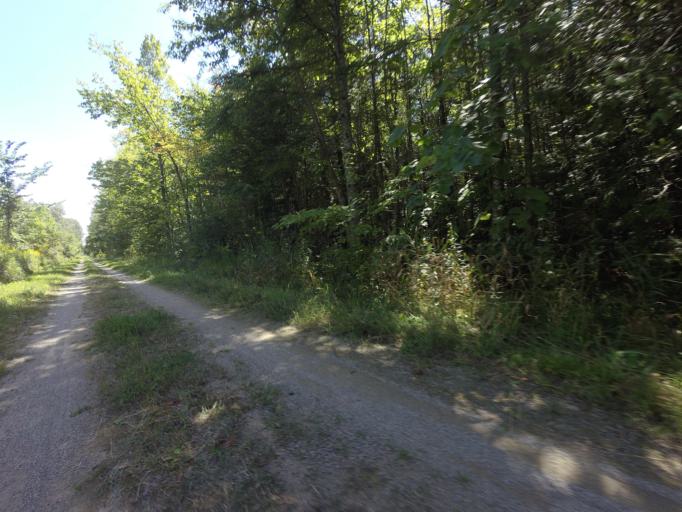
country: CA
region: Ontario
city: Orangeville
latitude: 43.7763
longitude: -80.2015
